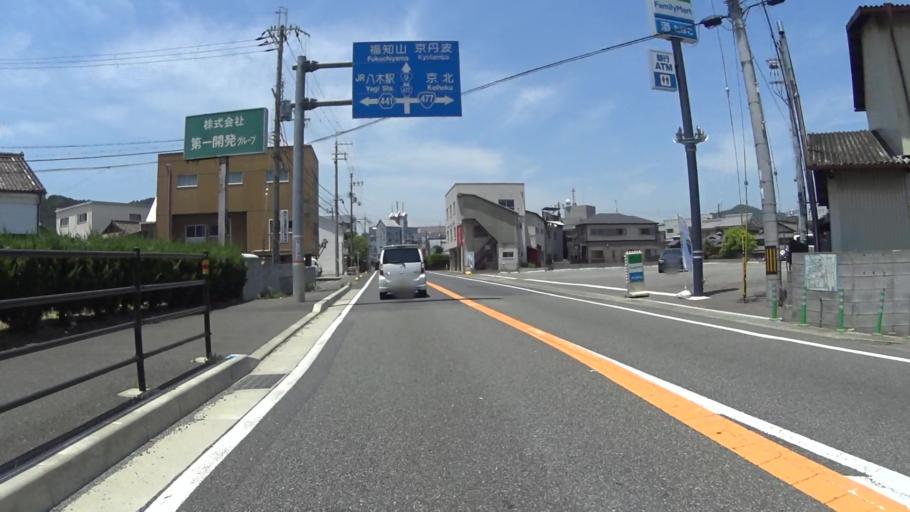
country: JP
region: Kyoto
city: Kameoka
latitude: 35.0690
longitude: 135.5337
